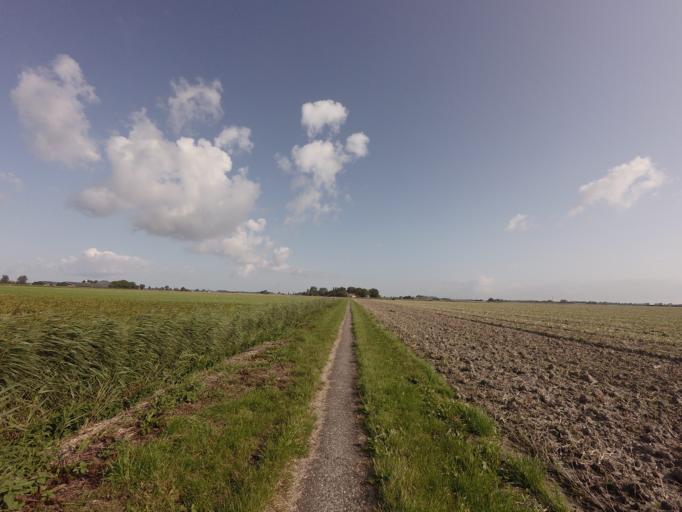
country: NL
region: Friesland
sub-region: Gemeente Franekeradeel
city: Franeker
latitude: 53.2062
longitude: 5.5647
